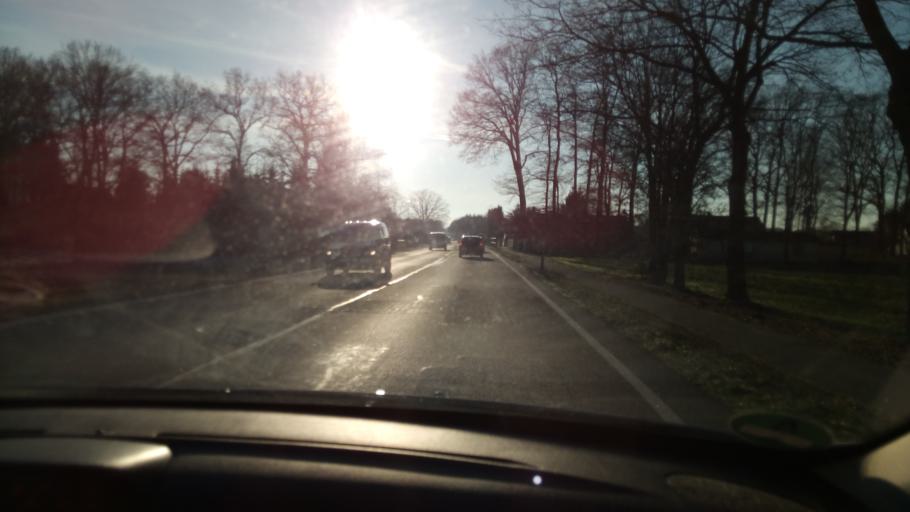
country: DE
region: Lower Saxony
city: Brietlingen
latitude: 53.3223
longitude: 10.4388
